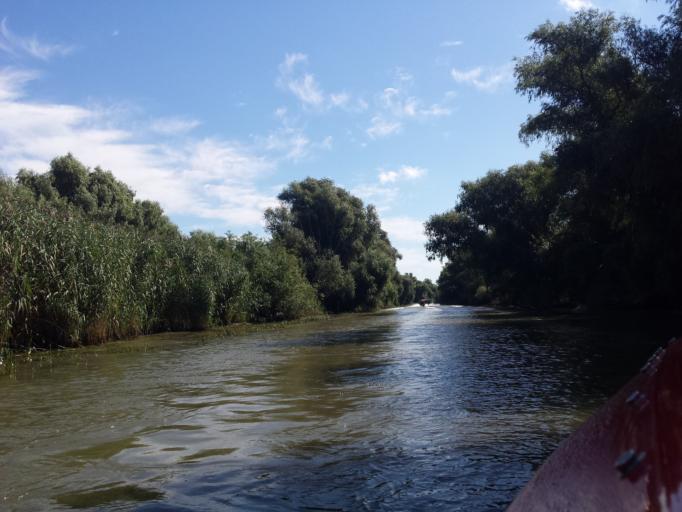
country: RO
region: Tulcea
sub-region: Comuna Mahmudia
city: Mahmudia
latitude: 45.2388
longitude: 29.1214
